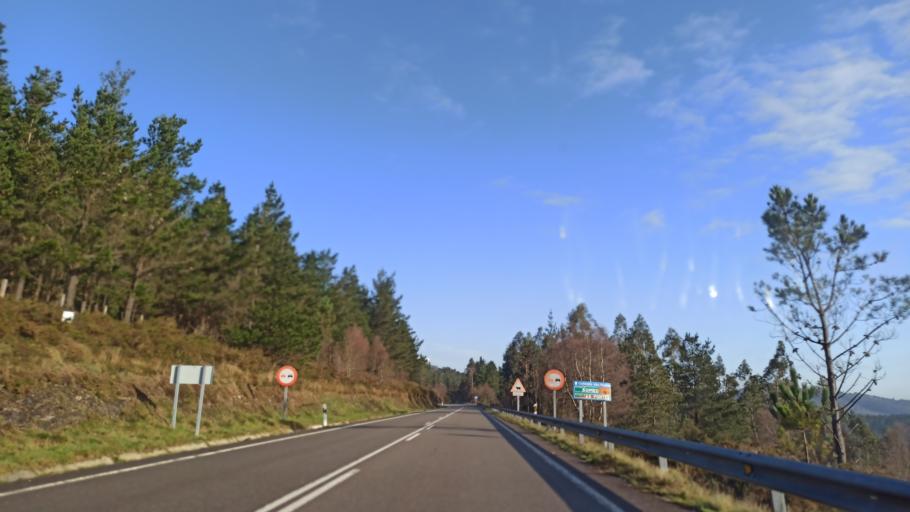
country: ES
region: Galicia
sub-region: Provincia da Coruna
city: As Pontes de Garcia Rodriguez
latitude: 43.4894
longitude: -7.8362
